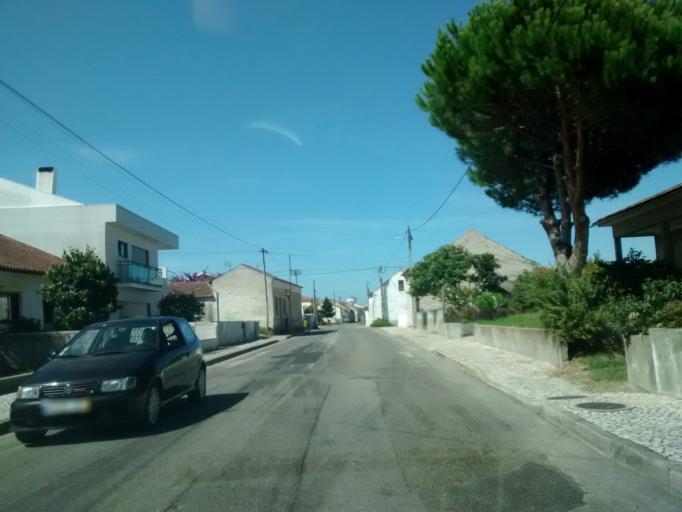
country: PT
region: Coimbra
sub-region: Mira
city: Mira
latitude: 40.4362
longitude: -8.7216
